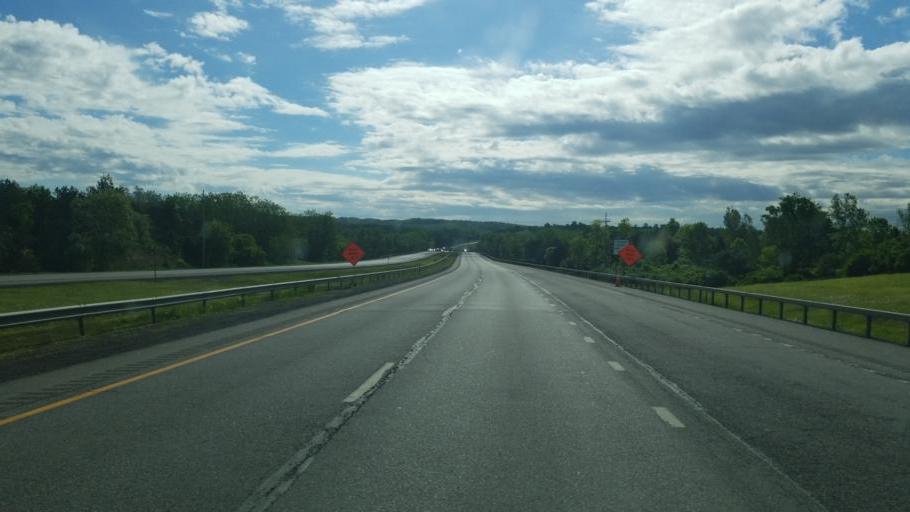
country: US
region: New York
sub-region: Ontario County
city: Victor
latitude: 43.0145
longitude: -77.4759
